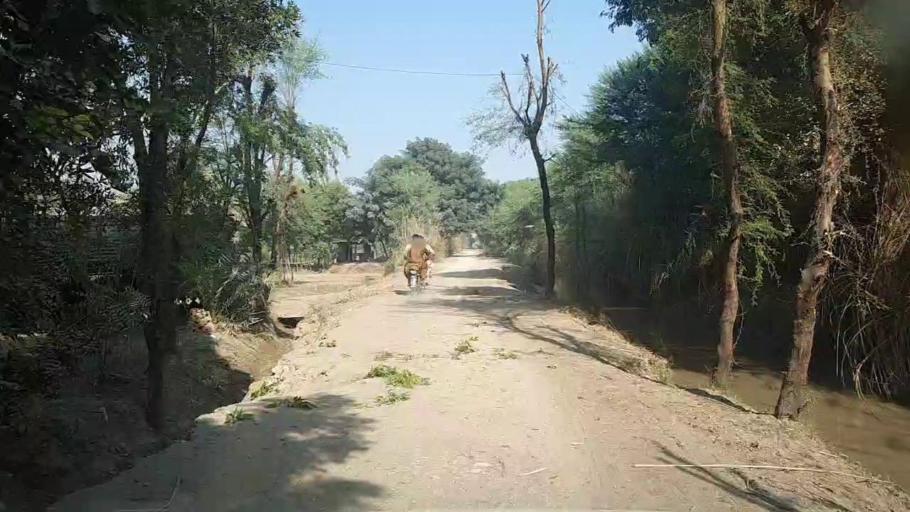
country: PK
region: Sindh
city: Karaundi
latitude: 26.9619
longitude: 68.4209
